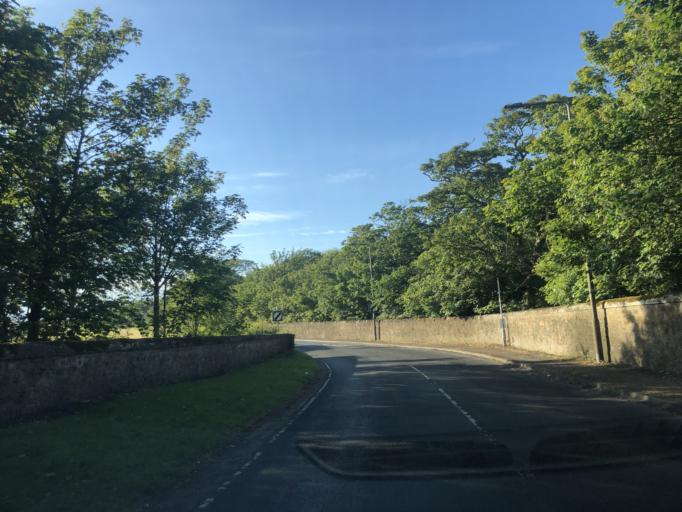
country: GB
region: Scotland
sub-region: Fife
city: Saint Monance
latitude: 56.1936
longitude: -2.8222
